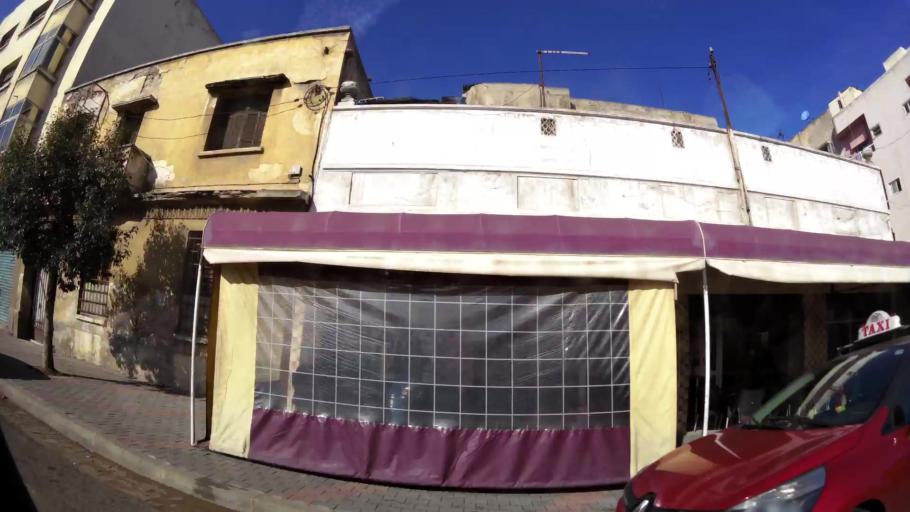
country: MA
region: Grand Casablanca
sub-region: Casablanca
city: Casablanca
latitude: 33.6017
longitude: -7.5786
